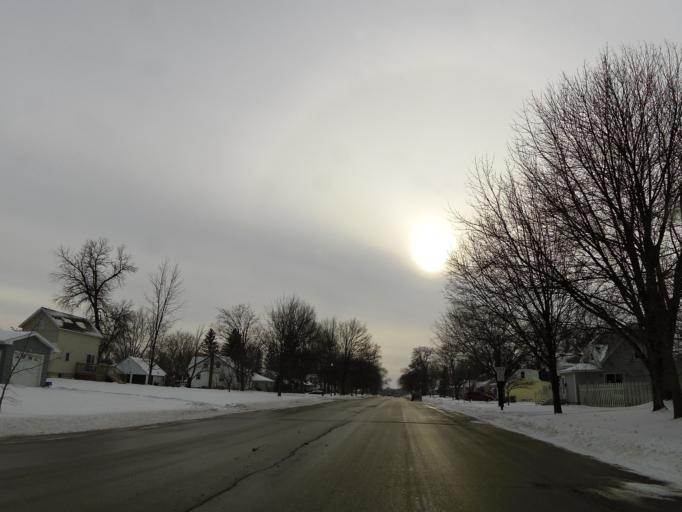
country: US
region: Minnesota
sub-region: McLeod County
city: Hutchinson
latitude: 44.8988
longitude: -94.3601
